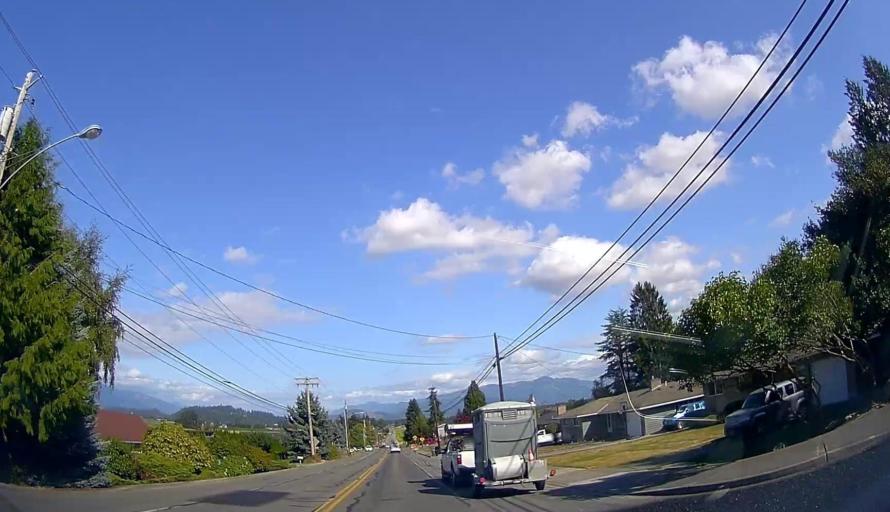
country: US
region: Washington
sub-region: Skagit County
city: Burlington
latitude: 48.4721
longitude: -122.3786
